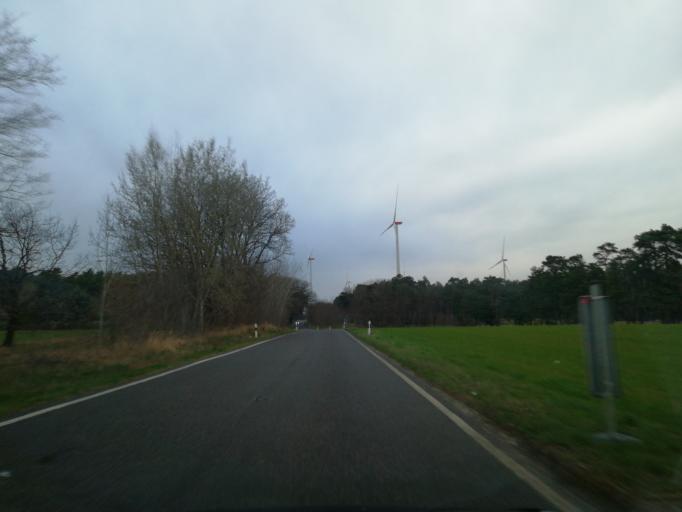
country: DE
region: Brandenburg
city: Vetschau
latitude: 51.7468
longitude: 14.0960
